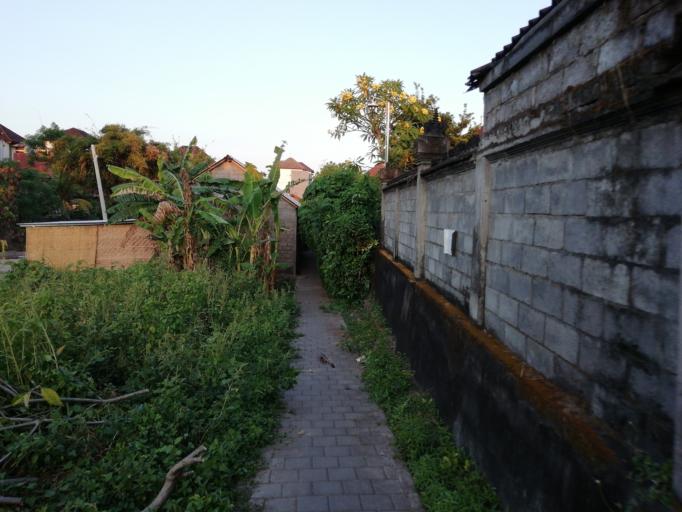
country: ID
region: Bali
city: Denpasar
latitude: -8.6408
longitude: 115.2131
